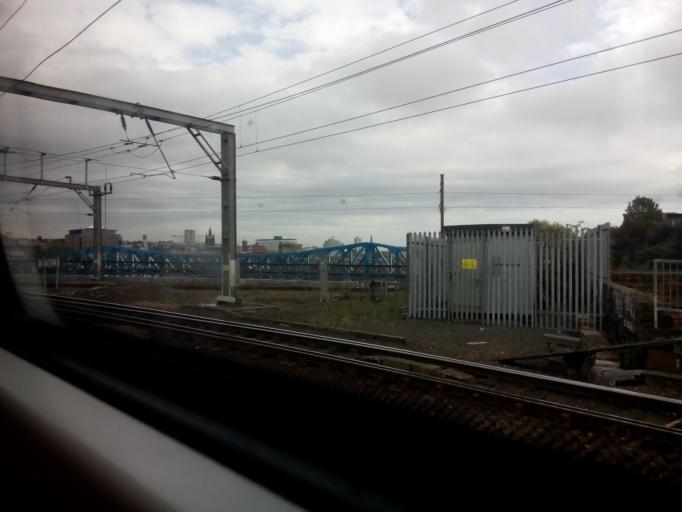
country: GB
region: England
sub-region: Newcastle upon Tyne
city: Newcastle upon Tyne
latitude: 54.9620
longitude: -1.6151
